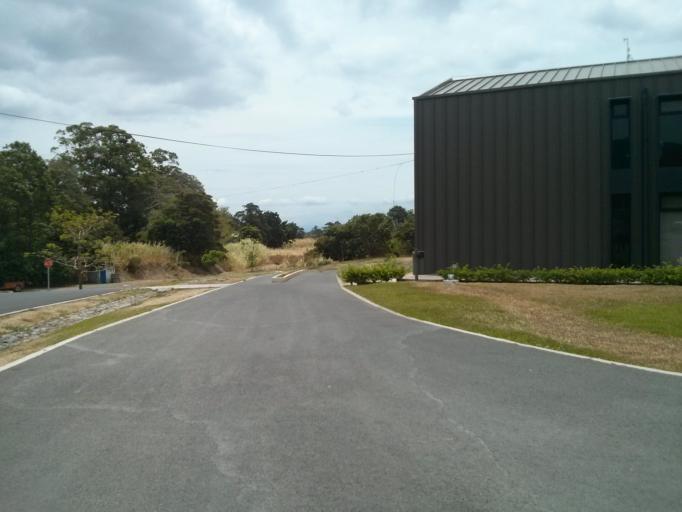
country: CR
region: San Jose
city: Patarra
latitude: 9.8897
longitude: -84.0367
